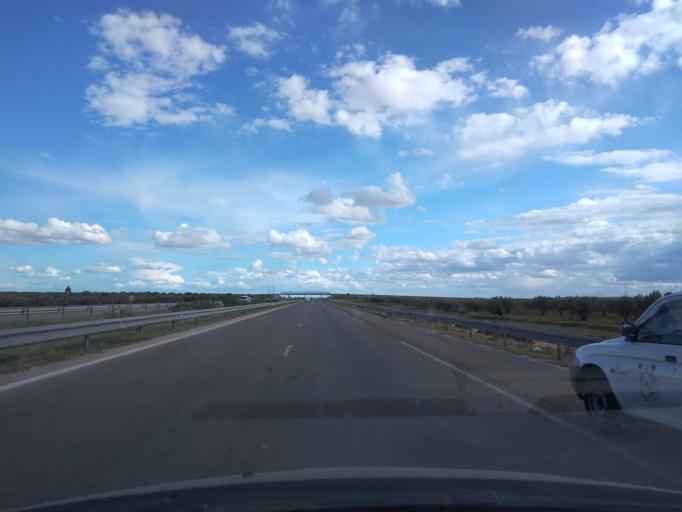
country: TN
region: Al Munastir
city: Manzil Kamil
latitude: 35.6385
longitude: 10.5808
